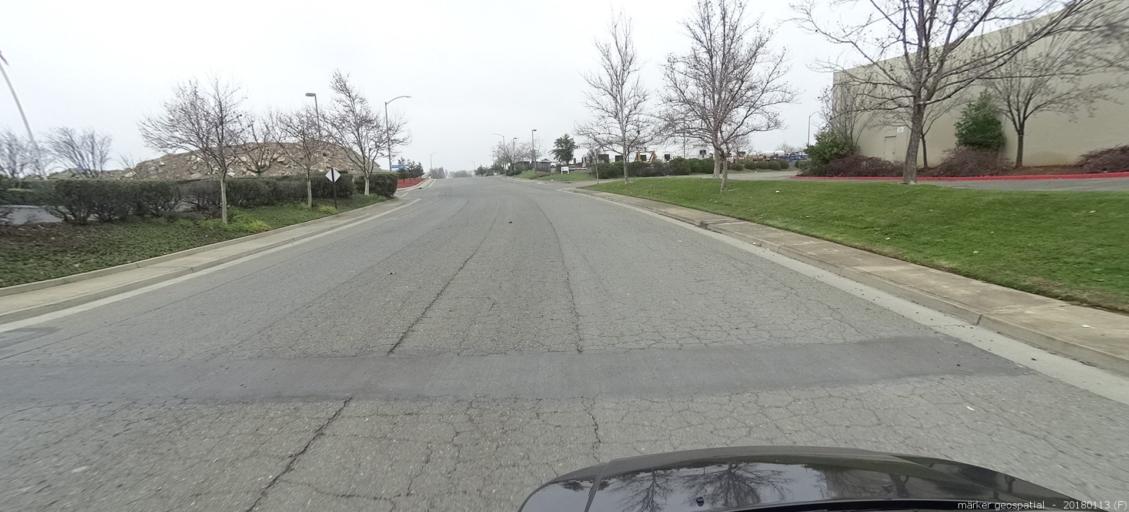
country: US
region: California
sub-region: Sacramento County
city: Gold River
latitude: 38.5785
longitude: -121.2550
